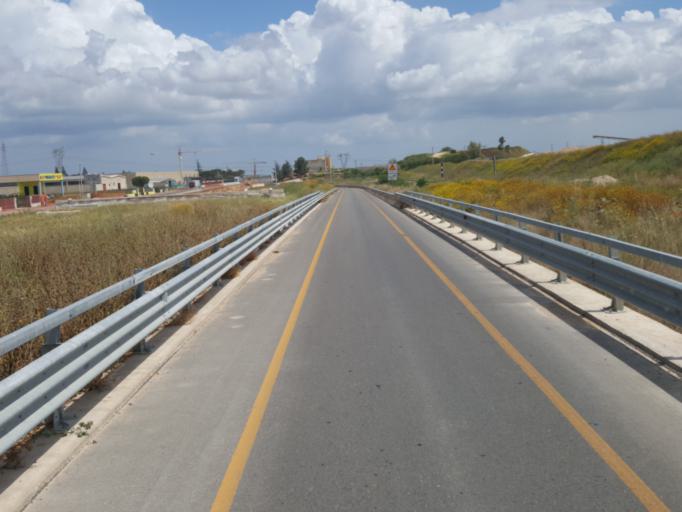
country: IT
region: Apulia
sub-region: Provincia di Bari
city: Palo del Colle
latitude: 41.0671
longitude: 16.7296
